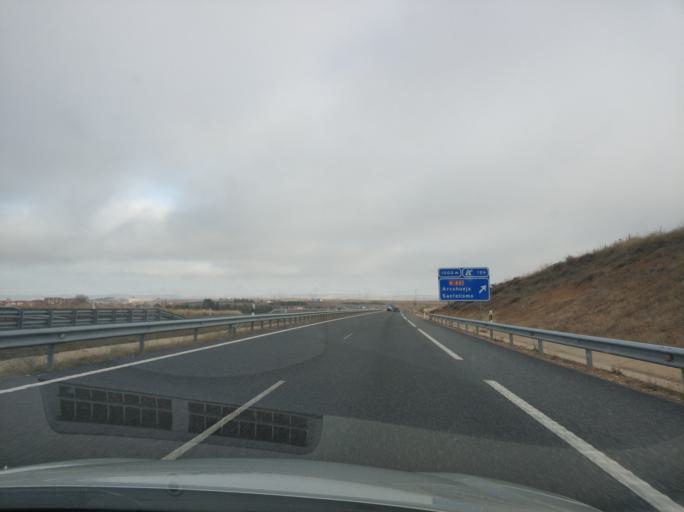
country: ES
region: Castille and Leon
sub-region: Provincia de Leon
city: Valdefresno
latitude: 42.5627
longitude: -5.5078
